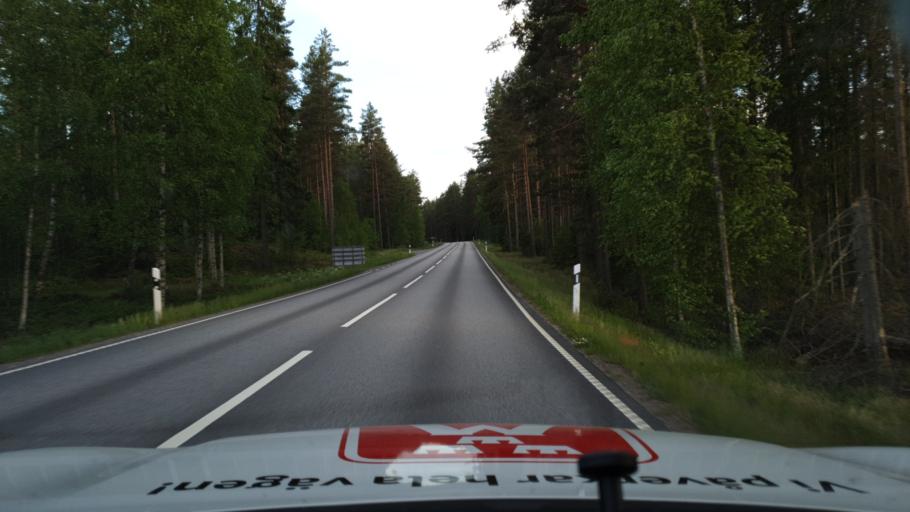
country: SE
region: OErebro
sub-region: Hallsbergs Kommun
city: Palsboda
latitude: 58.8729
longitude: 15.4158
